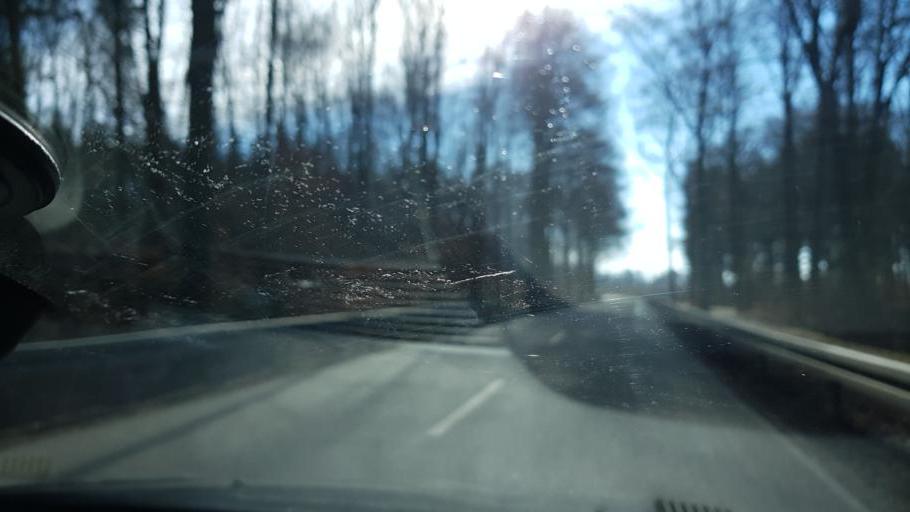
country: DE
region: Bavaria
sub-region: Upper Bavaria
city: Oberschweinbach
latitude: 48.2283
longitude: 11.1703
